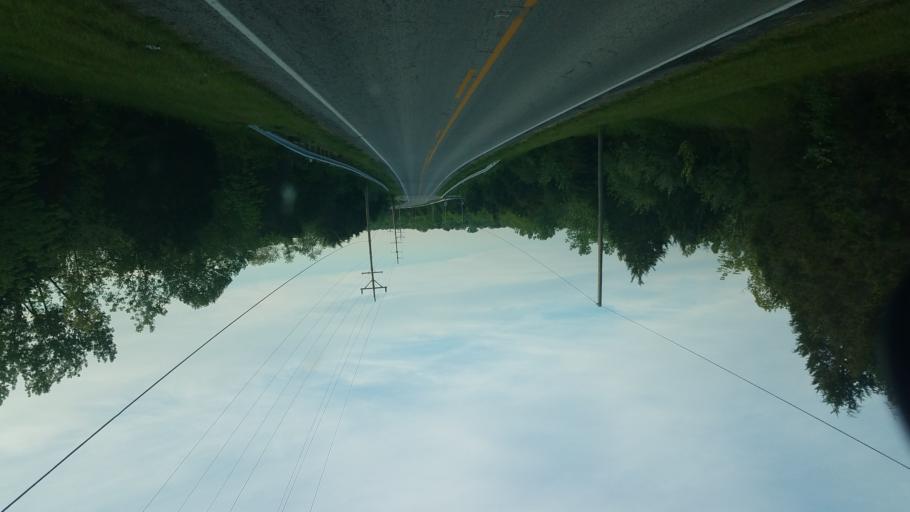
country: US
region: Ohio
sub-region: Highland County
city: Greenfield
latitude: 39.2807
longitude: -83.4158
